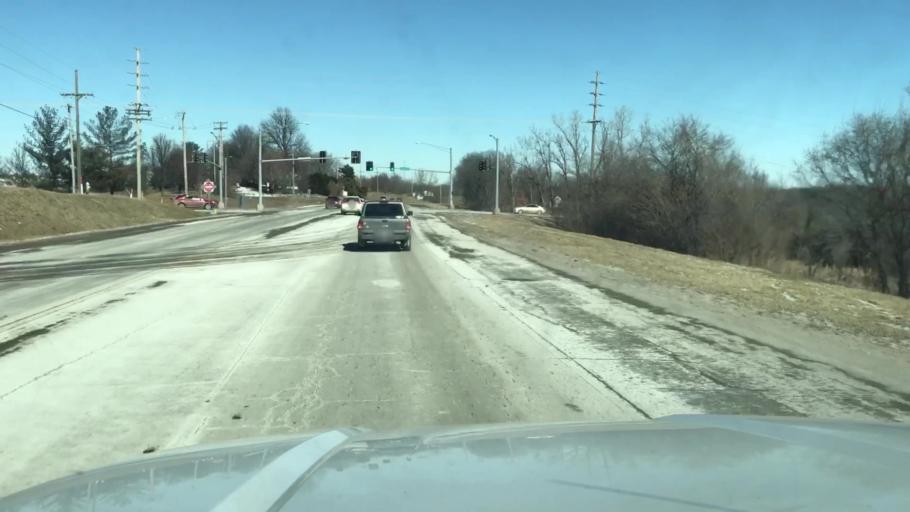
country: US
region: Missouri
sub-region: Andrew County
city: Country Club Village
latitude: 39.8058
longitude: -94.8107
